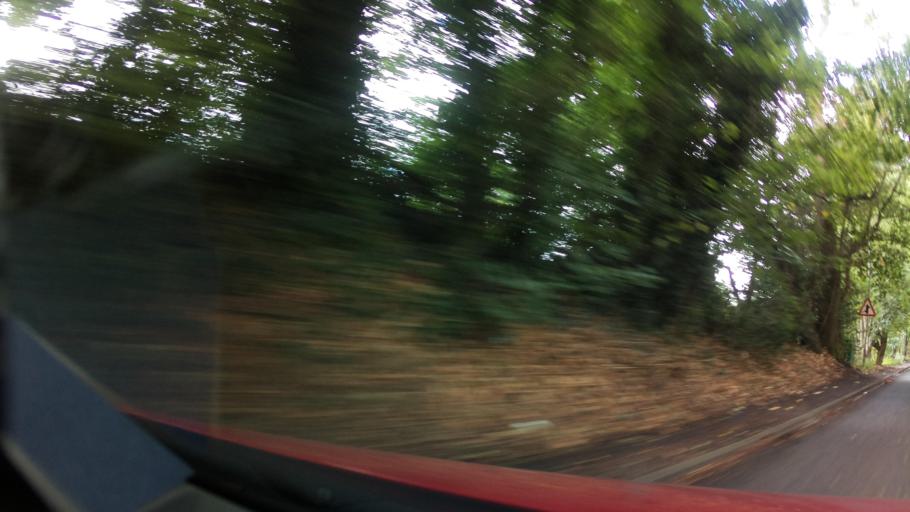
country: GB
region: England
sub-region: Staffordshire
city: Newcastle under Lyme
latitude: 52.9719
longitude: -2.2105
